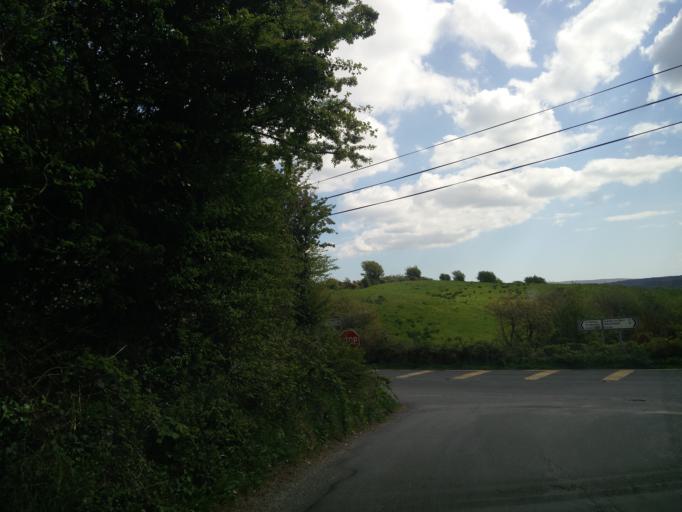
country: IE
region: Connaught
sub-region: Maigh Eo
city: Westport
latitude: 53.7875
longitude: -9.4628
